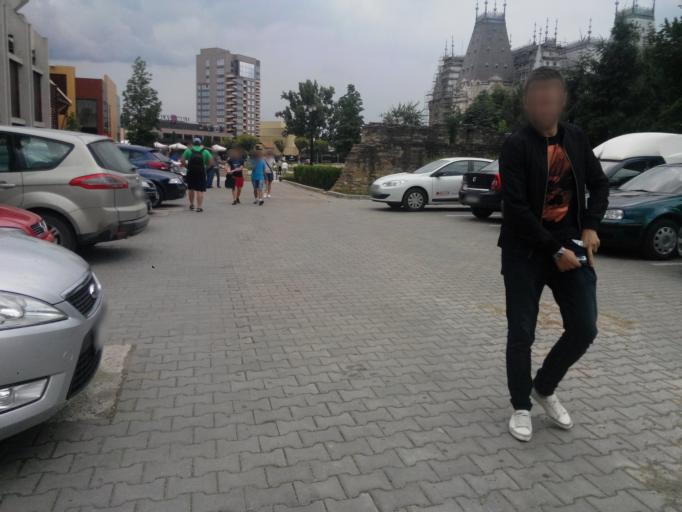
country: RO
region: Iasi
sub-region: Municipiul Iasi
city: Iasi
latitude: 47.1590
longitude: 27.5880
